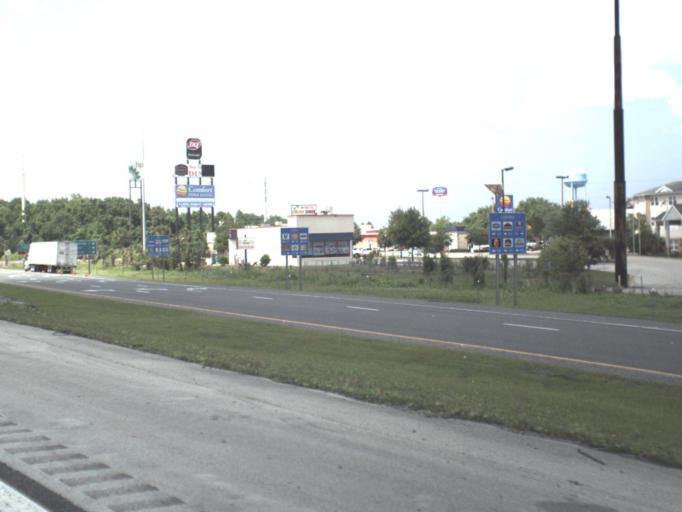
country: US
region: Florida
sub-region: Saint Johns County
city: Saint Augustine
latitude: 29.9148
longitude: -81.4110
